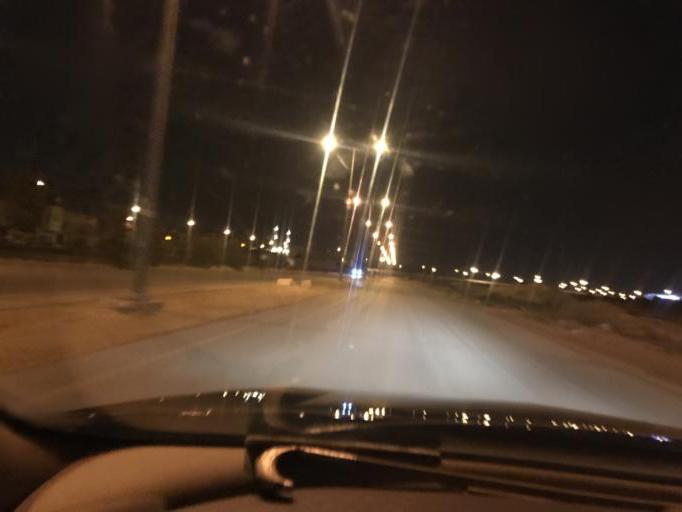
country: SA
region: Ar Riyad
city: Riyadh
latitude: 24.8180
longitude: 46.7218
